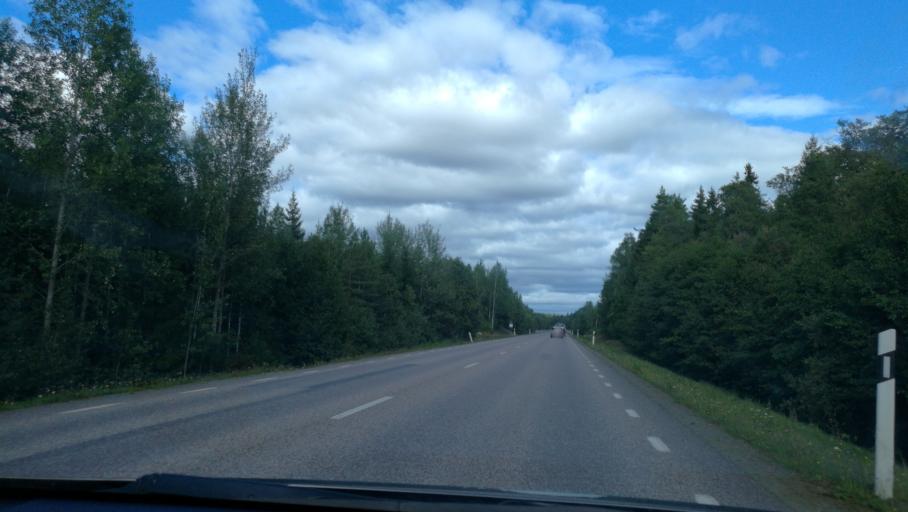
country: SE
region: Soedermanland
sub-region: Eskilstuna Kommun
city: Kvicksund
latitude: 59.5098
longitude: 16.3116
